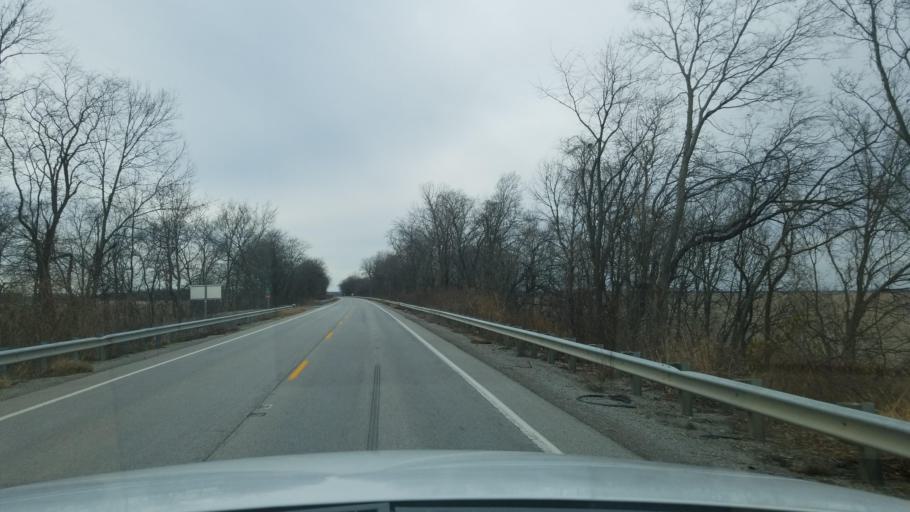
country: US
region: Indiana
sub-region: Posey County
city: Mount Vernon
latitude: 37.9437
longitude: -88.0433
